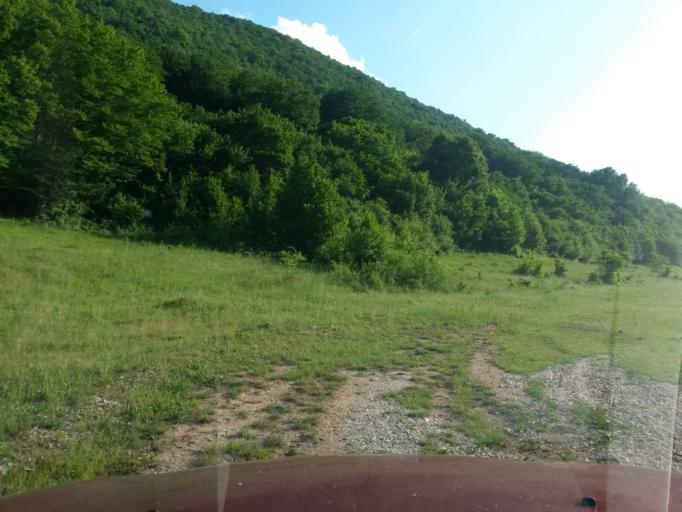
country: SK
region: Kosicky
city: Roznava
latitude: 48.5824
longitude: 20.6791
